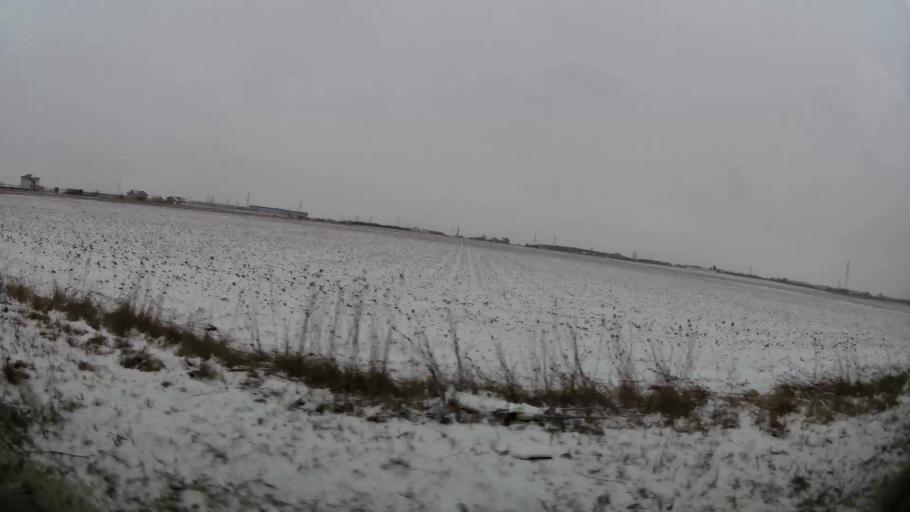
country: RO
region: Dambovita
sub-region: Comuna Ulmi
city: Ulmi
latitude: 44.8898
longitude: 25.5201
